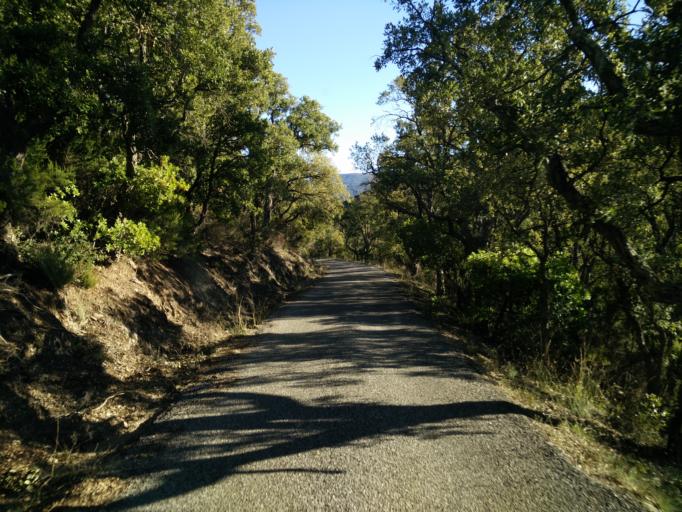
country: FR
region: Provence-Alpes-Cote d'Azur
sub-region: Departement du Var
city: Collobrieres
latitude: 43.2617
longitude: 6.2983
